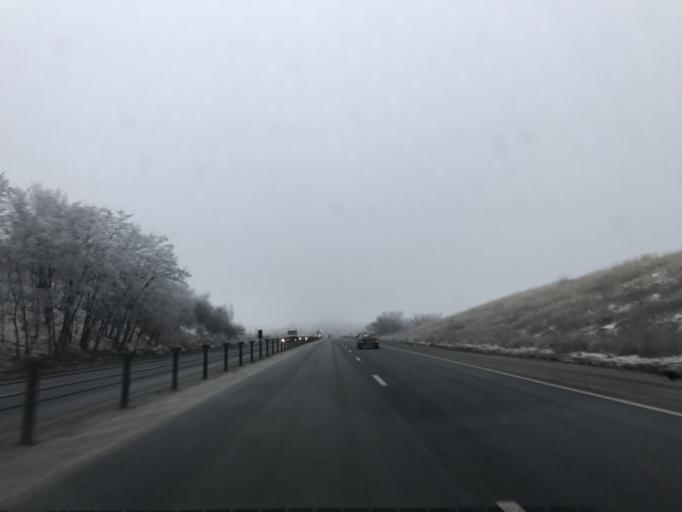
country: RU
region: Rostov
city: Grushevskaya
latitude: 47.4373
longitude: 39.9751
